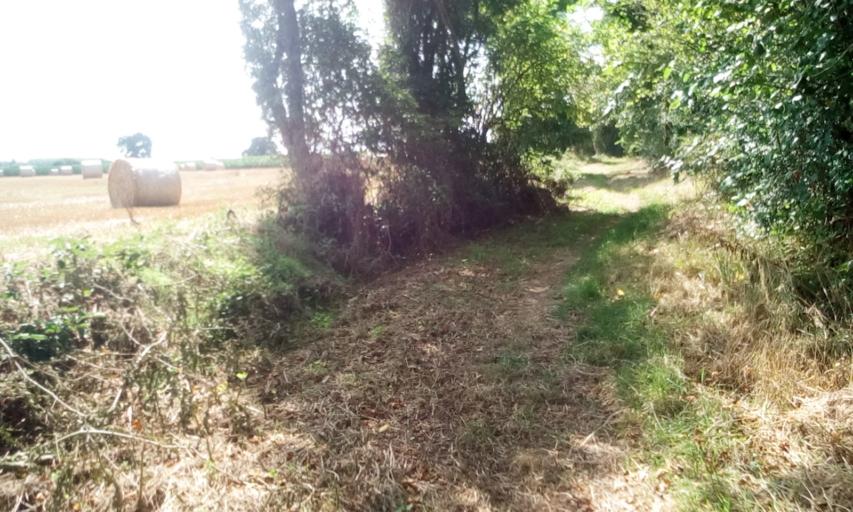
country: FR
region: Lower Normandy
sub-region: Departement du Calvados
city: Argences
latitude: 49.1473
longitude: -0.1206
